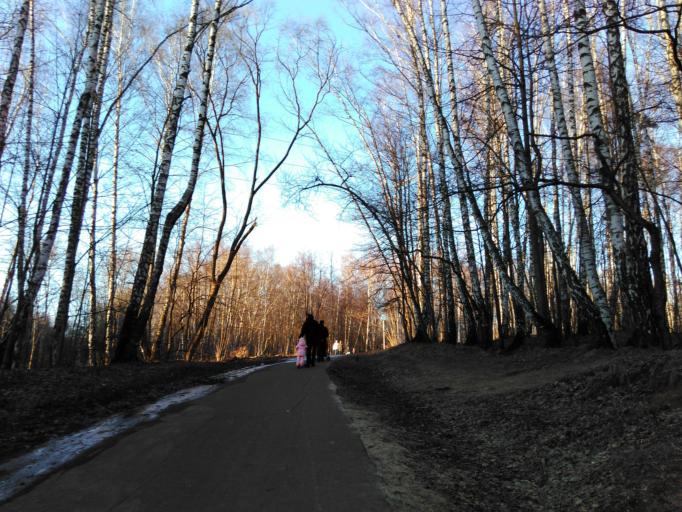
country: RU
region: Moscow
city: Zyuzino
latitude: 55.6380
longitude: 37.5636
